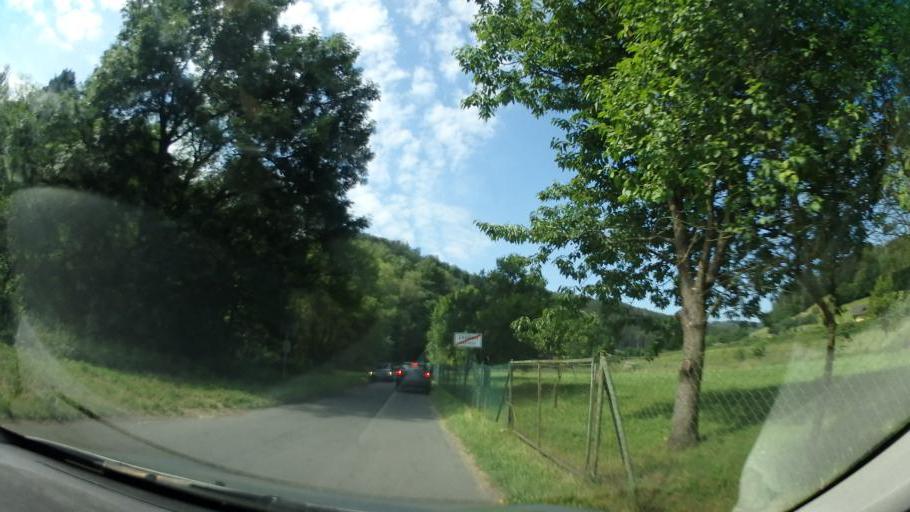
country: CZ
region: Olomoucky
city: Zabreh
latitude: 49.8648
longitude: 16.8175
